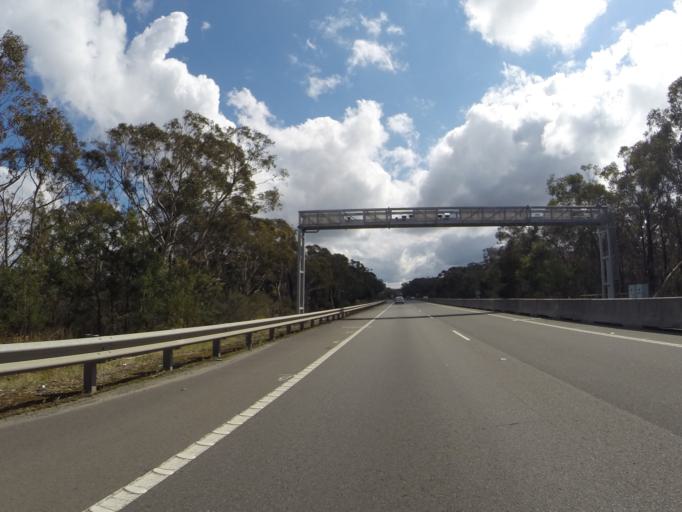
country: AU
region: New South Wales
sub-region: Wollongong
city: Mount Keira
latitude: -34.3731
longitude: 150.8295
